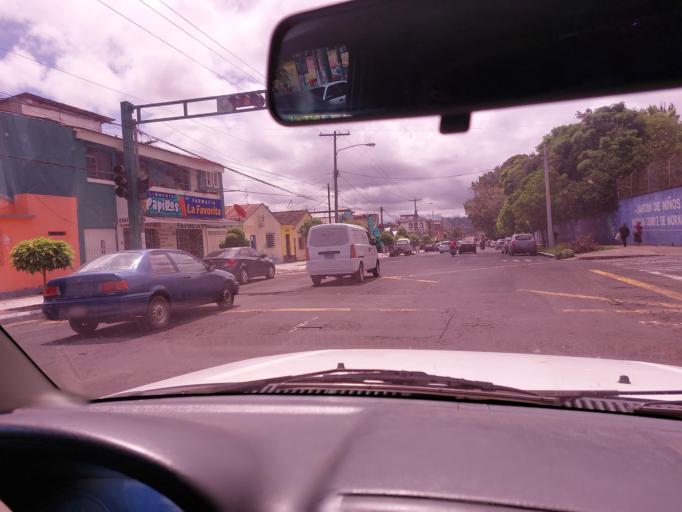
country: GT
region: Guatemala
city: Guatemala City
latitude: 14.6249
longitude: -90.5023
